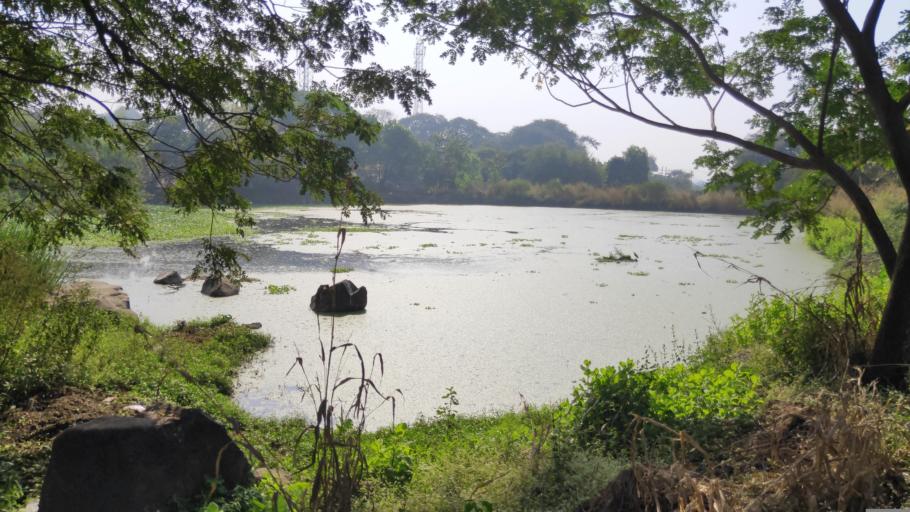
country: IN
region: Maharashtra
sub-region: Thane
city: Bhiwandi
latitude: 19.3126
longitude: 73.0343
